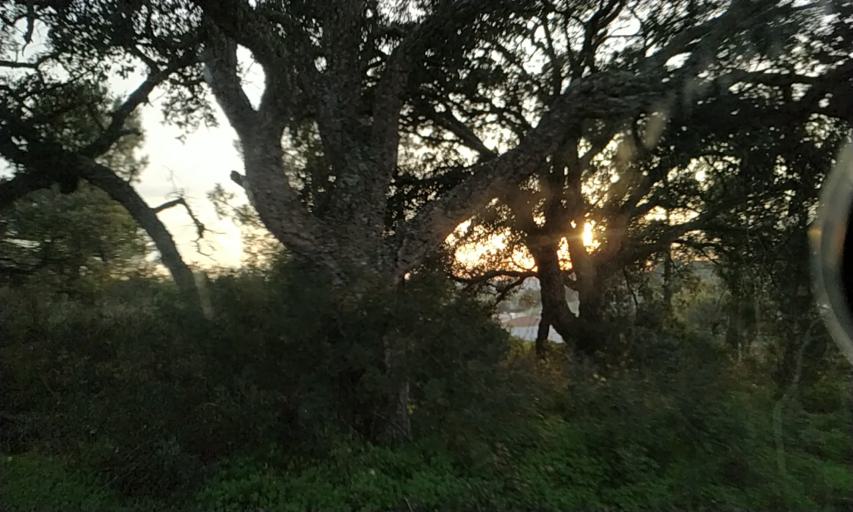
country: PT
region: Setubal
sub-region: Setubal
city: Setubal
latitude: 38.5249
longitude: -8.8551
